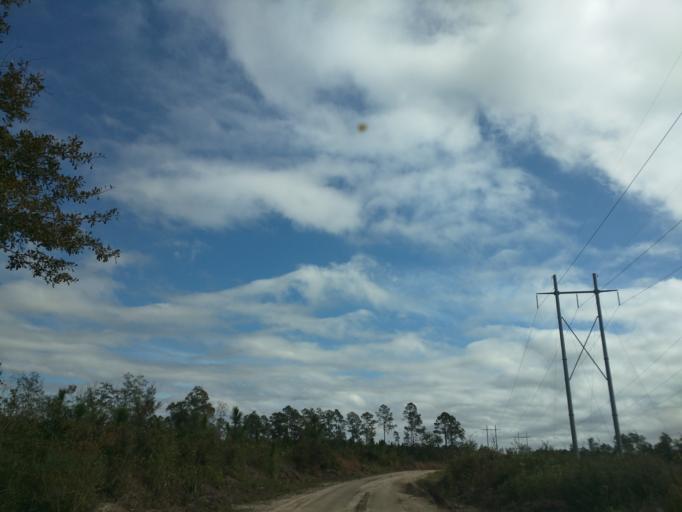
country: US
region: Florida
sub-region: Escambia County
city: Cantonment
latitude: 30.5314
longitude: -87.4308
